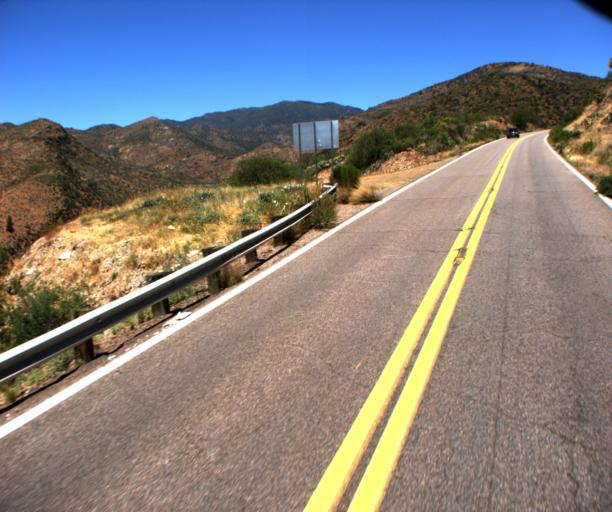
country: US
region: Arizona
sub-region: Pinal County
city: Kearny
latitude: 33.2017
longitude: -110.8039
